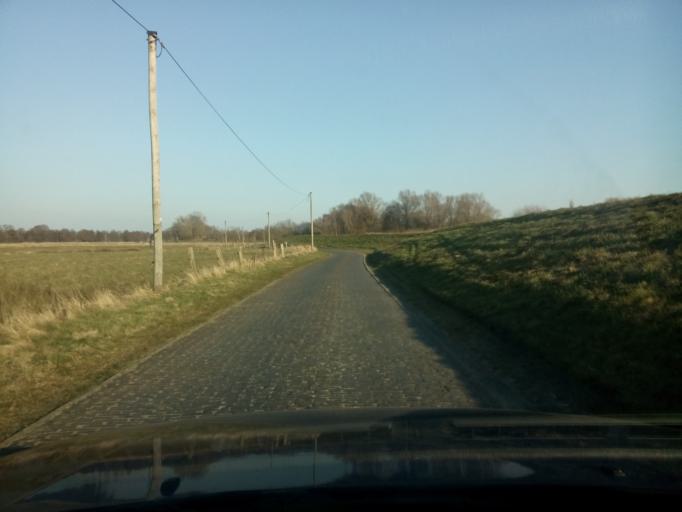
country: DE
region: Lower Saxony
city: Lilienthal
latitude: 53.1348
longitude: 8.8761
